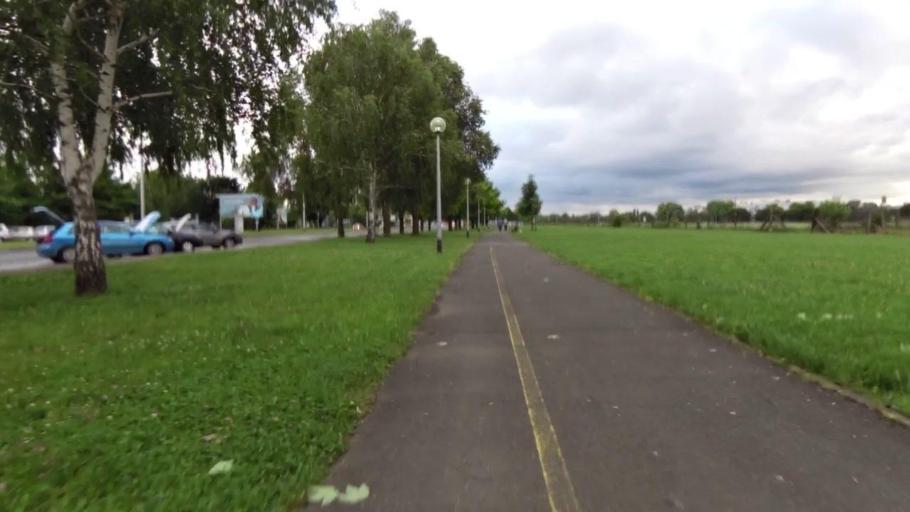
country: HR
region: Grad Zagreb
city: Dubrava
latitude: 45.8276
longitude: 16.0349
